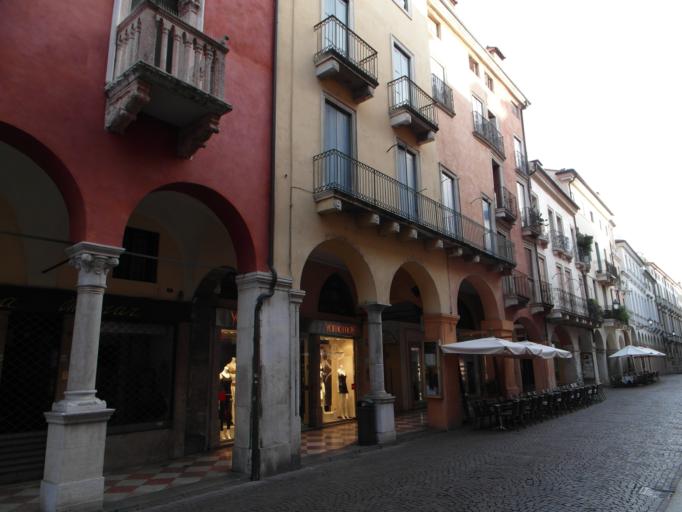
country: IT
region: Veneto
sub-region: Provincia di Vicenza
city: Vicenza
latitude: 45.5477
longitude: 11.5442
